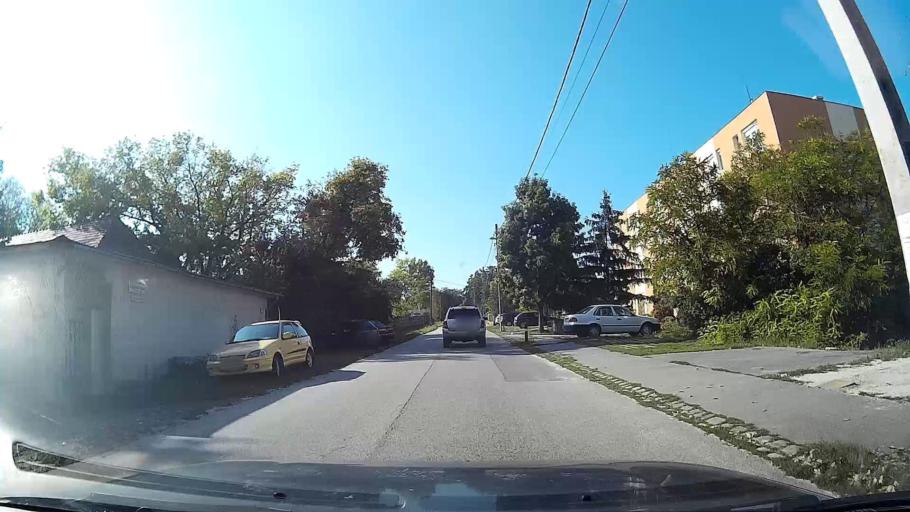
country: HU
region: Budapest
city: Budapest XXII. keruelet
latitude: 47.4158
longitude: 19.0102
